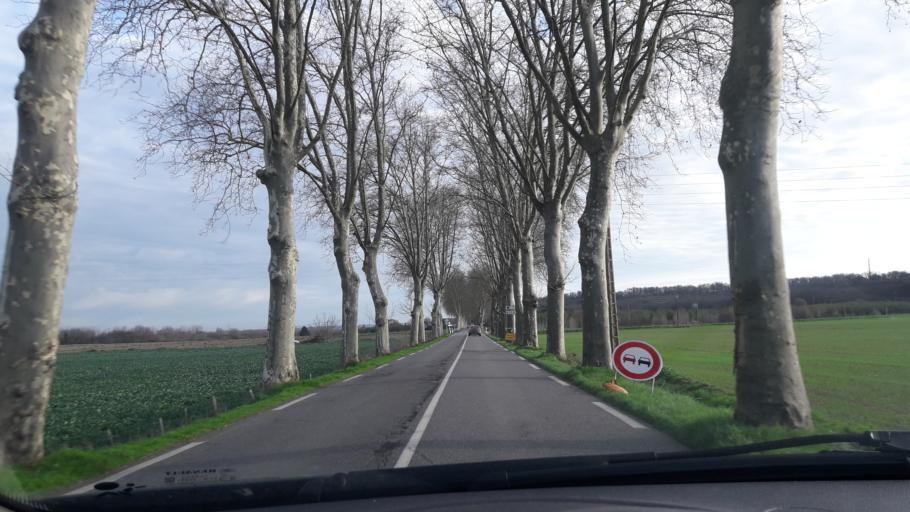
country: FR
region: Midi-Pyrenees
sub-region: Departement de la Haute-Garonne
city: Daux
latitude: 43.7236
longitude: 1.2461
